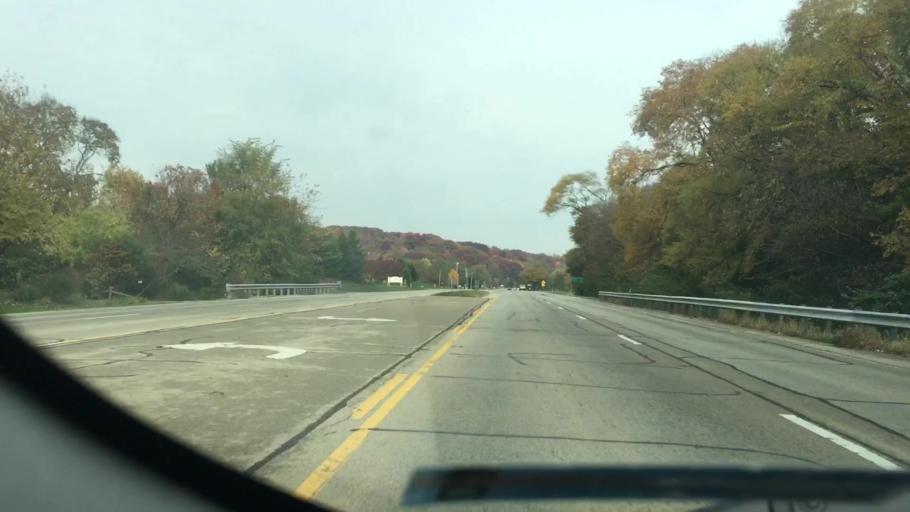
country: US
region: Illinois
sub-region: Peoria County
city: Peoria Heights
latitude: 40.7688
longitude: -89.5715
